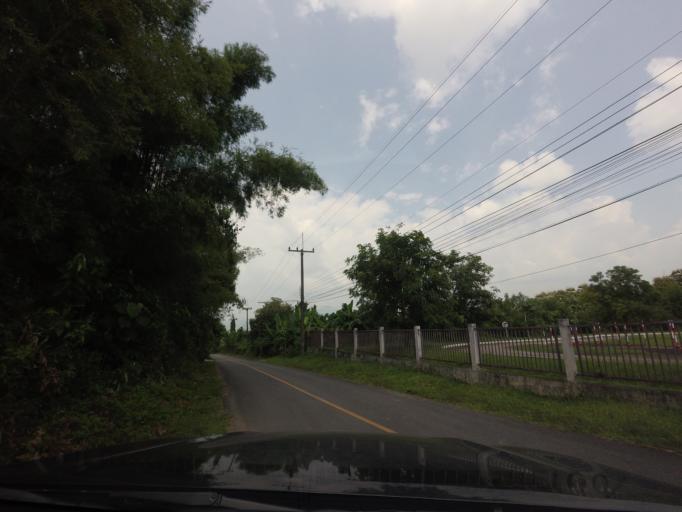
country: TH
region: Nan
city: Pua
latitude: 19.1683
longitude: 100.9273
